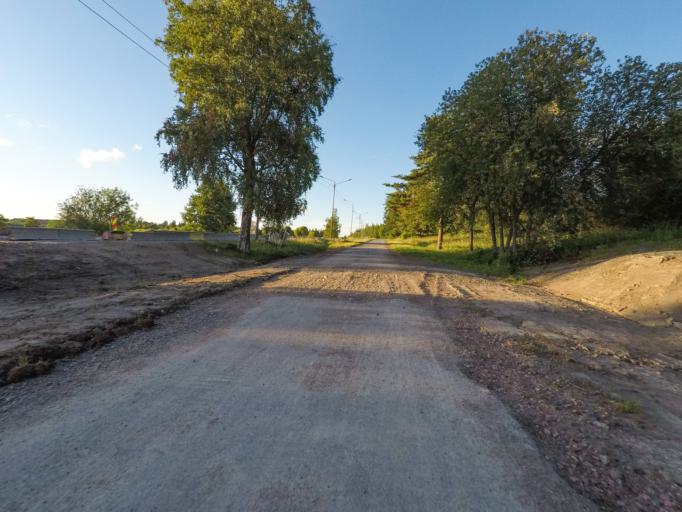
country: FI
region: South Karelia
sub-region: Imatra
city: Imatra
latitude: 61.2024
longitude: 28.7876
